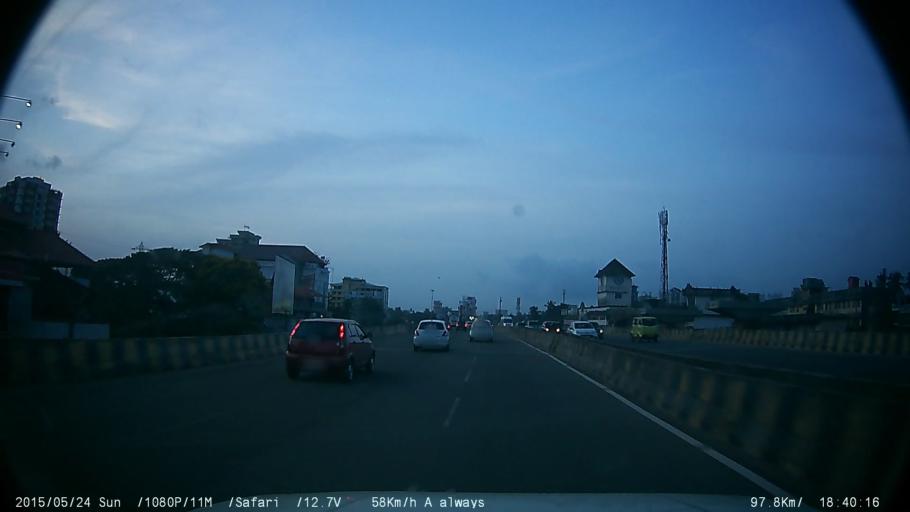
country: IN
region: Kerala
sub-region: Ernakulam
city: Aluva
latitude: 10.1061
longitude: 76.3499
